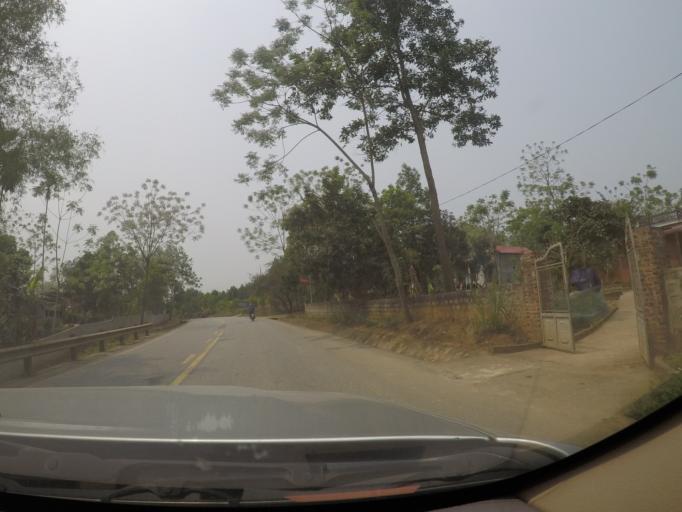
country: VN
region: Thanh Hoa
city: Thi Tran Ngoc Lac
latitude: 20.1359
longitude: 105.4160
